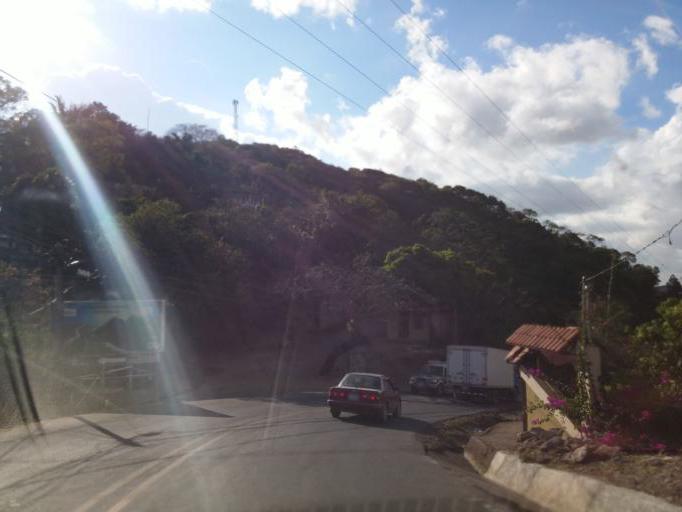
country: CR
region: San Jose
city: San Ignacio
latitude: 9.7959
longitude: -84.1553
